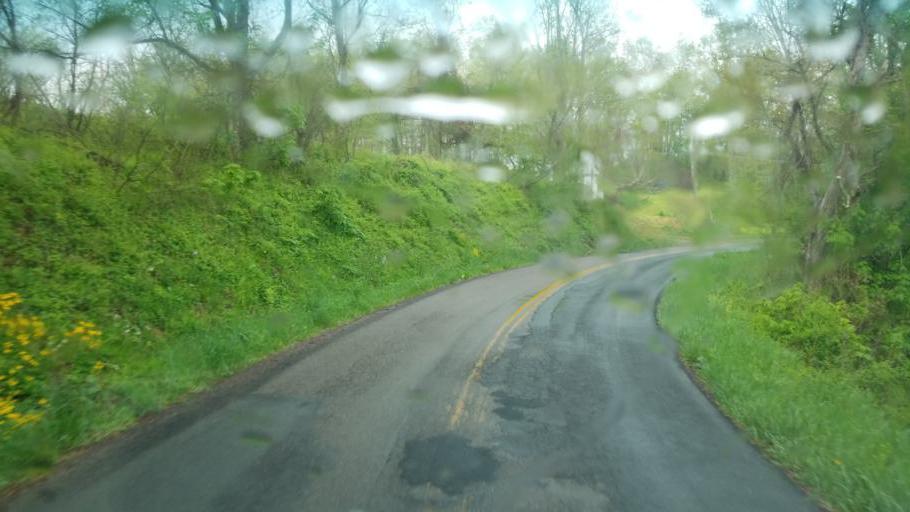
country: US
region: Virginia
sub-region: Smyth County
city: Adwolf
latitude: 36.7601
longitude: -81.5529
